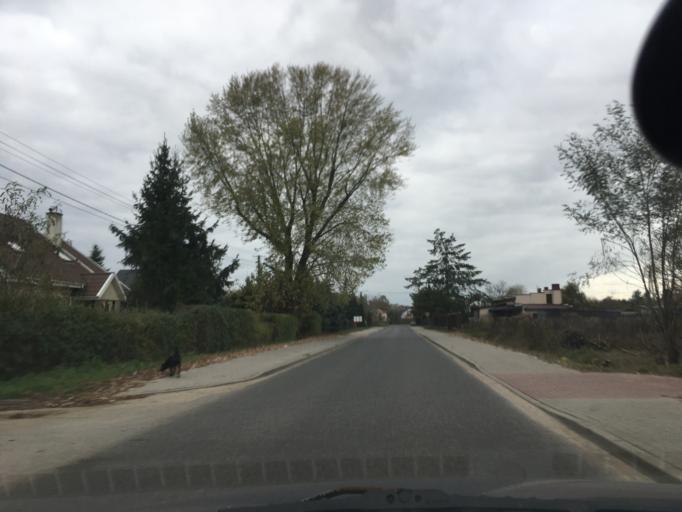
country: PL
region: Lodz Voivodeship
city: Zabia Wola
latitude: 52.0288
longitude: 20.6941
